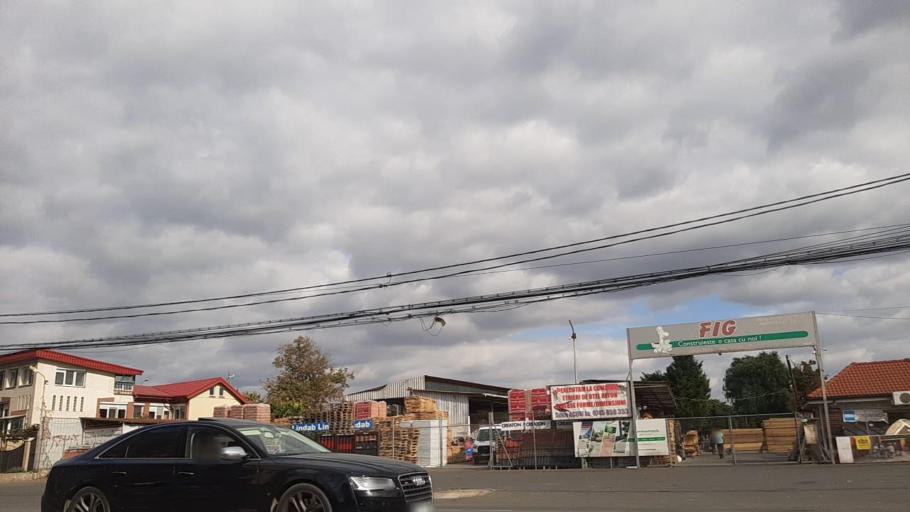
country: RO
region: Galati
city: Galati
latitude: 45.4518
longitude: 28.0347
